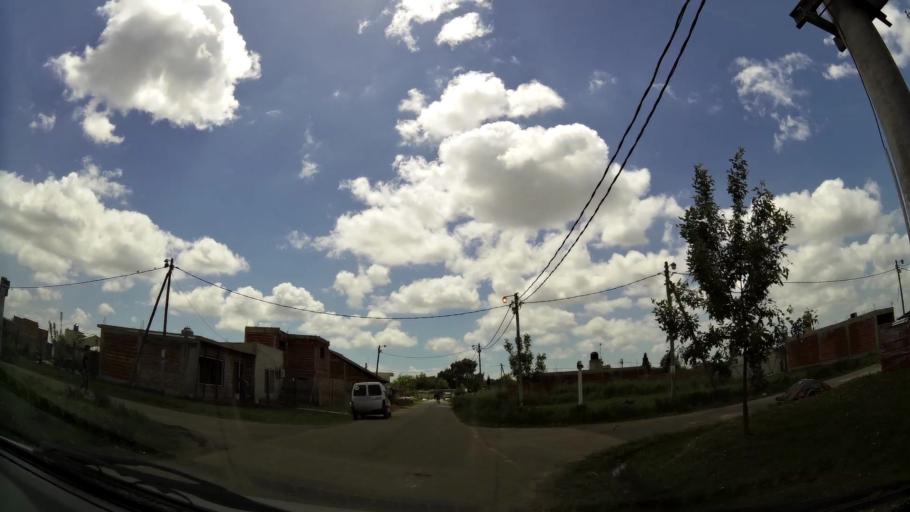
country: AR
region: Buenos Aires
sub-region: Partido de Quilmes
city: Quilmes
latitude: -34.8307
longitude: -58.2385
